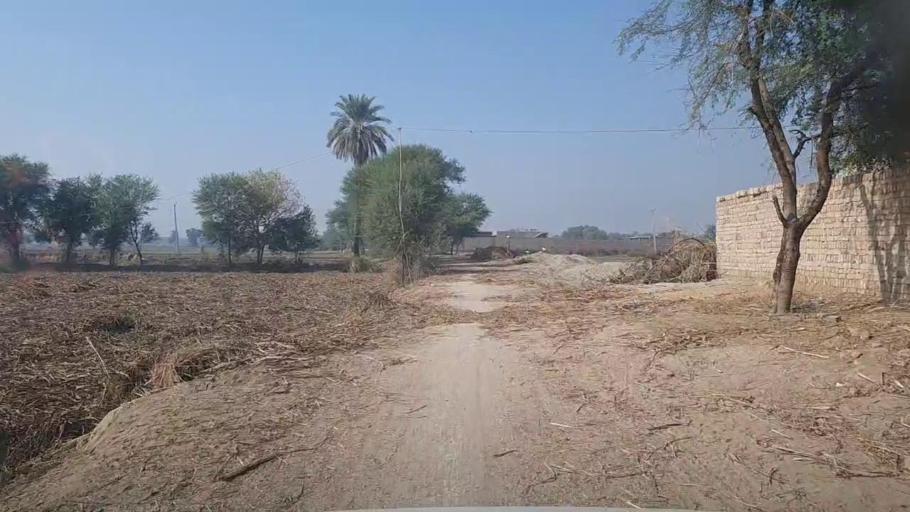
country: PK
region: Sindh
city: Kandiari
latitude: 26.9944
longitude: 68.4884
